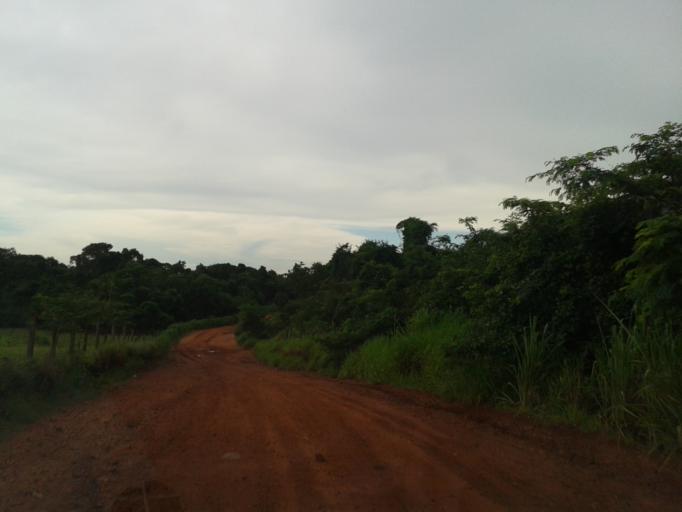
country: BR
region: Minas Gerais
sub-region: Santa Vitoria
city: Santa Vitoria
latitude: -19.1324
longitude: -50.5530
